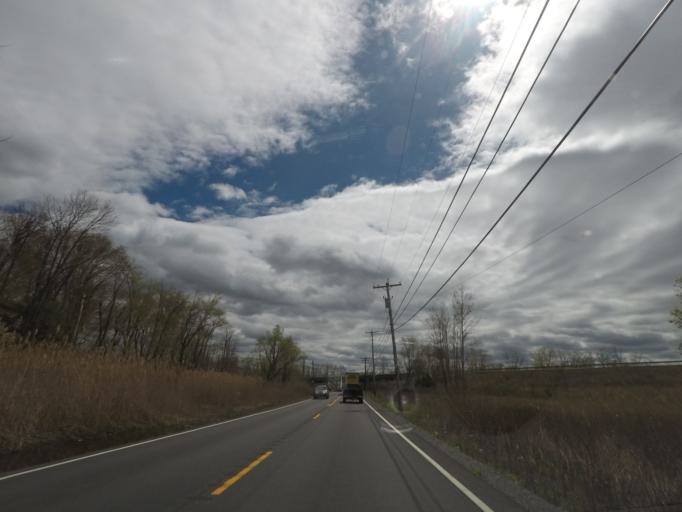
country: US
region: New York
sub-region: Rensselaer County
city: Castleton-on-Hudson
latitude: 42.5154
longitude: -73.7868
